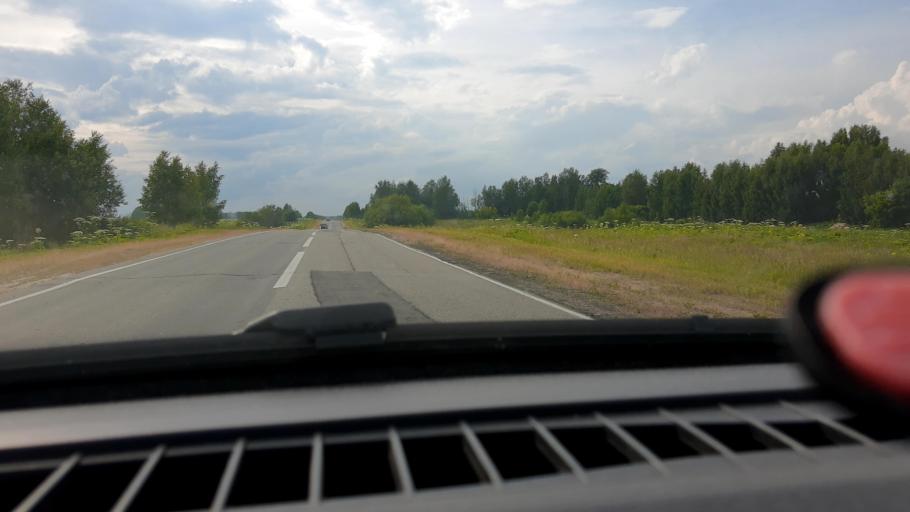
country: RU
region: Nizjnij Novgorod
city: Sitniki
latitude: 56.4963
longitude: 44.0043
